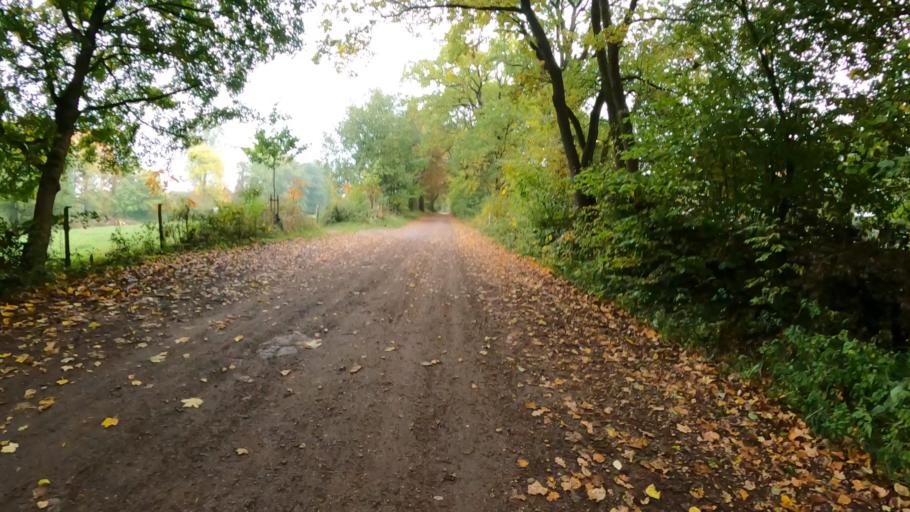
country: DE
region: Schleswig-Holstein
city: Ahrensburg
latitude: 53.6575
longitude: 10.1963
